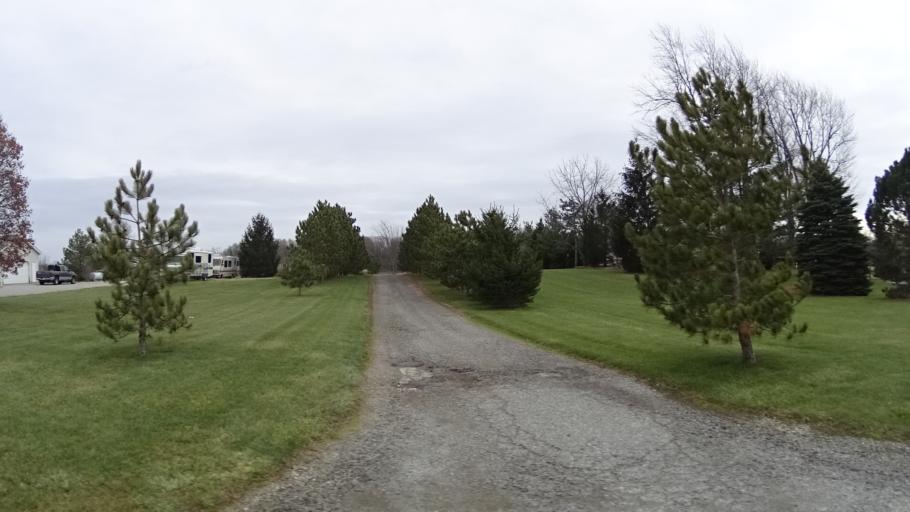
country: US
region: Ohio
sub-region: Lorain County
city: Wellington
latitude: 41.1854
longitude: -82.1931
